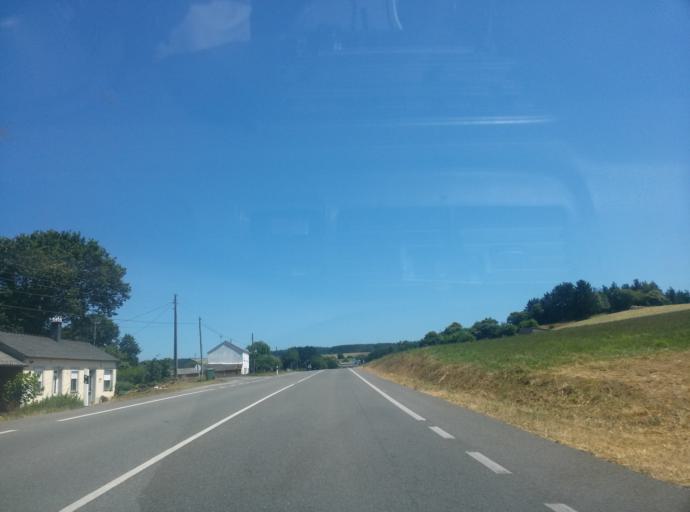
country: ES
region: Galicia
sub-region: Provincia de Lugo
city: Castro de Rei
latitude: 43.2329
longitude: -7.3797
